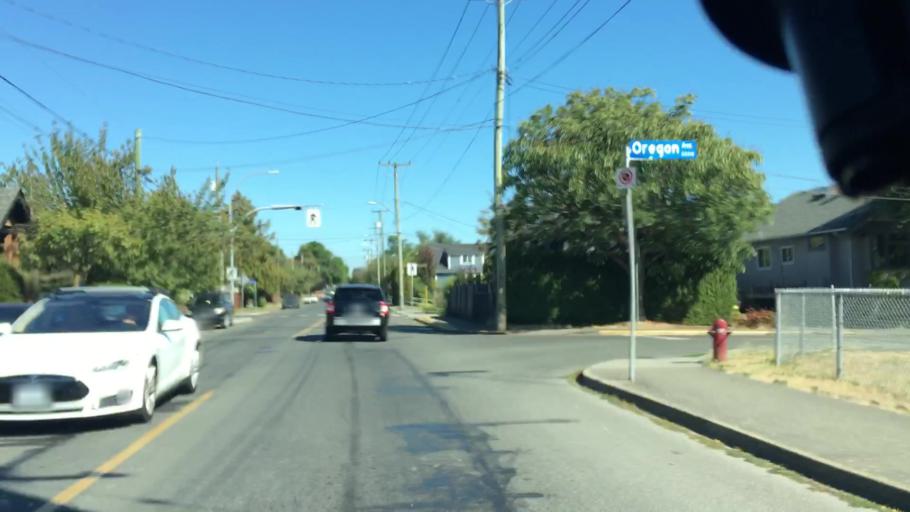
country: CA
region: British Columbia
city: Victoria
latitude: 48.4344
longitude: -123.3432
